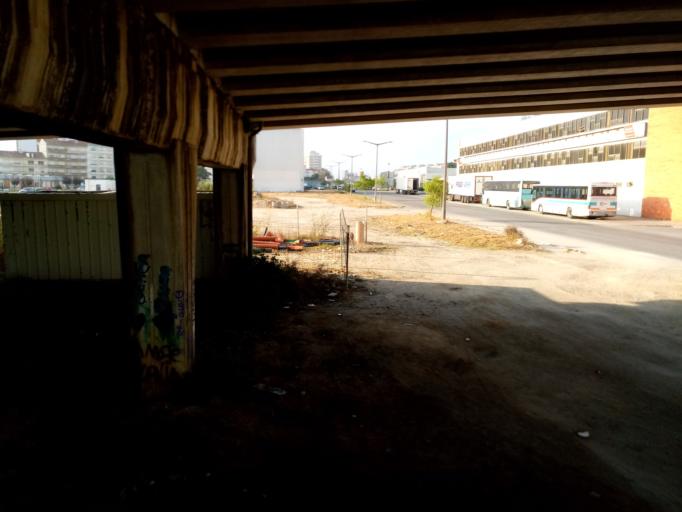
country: PT
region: Leiria
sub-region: Caldas da Rainha
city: Caldas da Rainha
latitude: 39.4129
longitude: -9.1407
